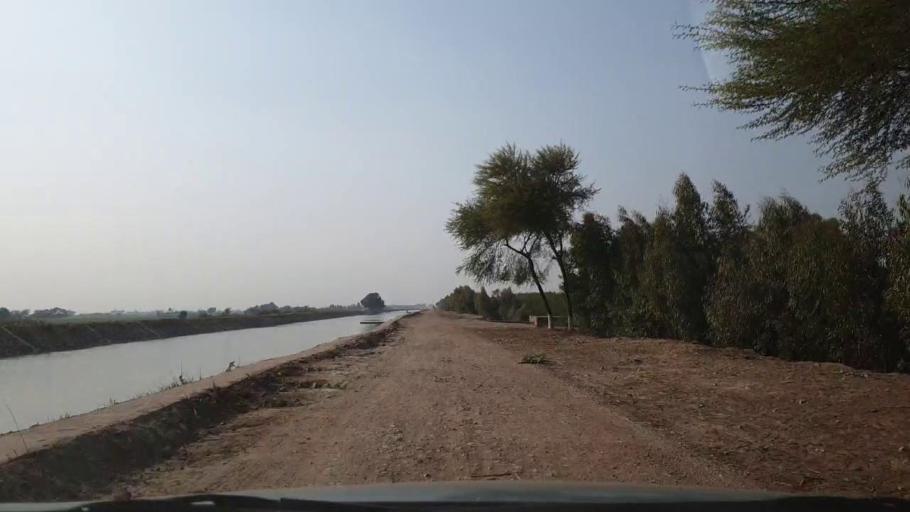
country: PK
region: Sindh
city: Matiari
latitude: 25.6404
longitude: 68.5836
